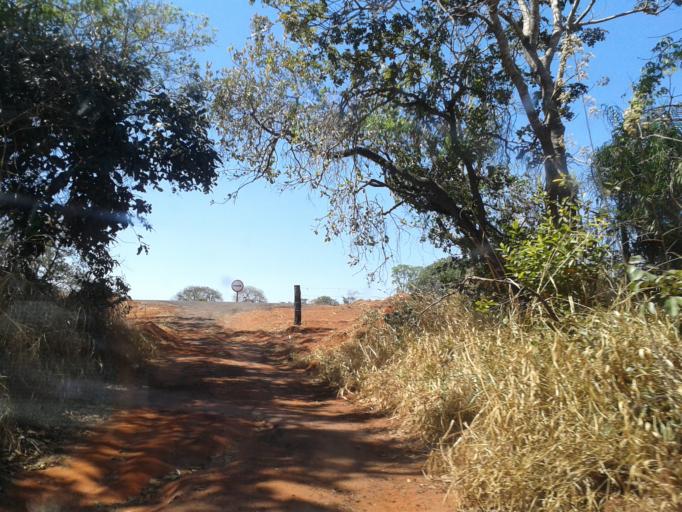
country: BR
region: Minas Gerais
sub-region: Monte Alegre De Minas
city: Monte Alegre de Minas
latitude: -18.8403
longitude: -49.0933
